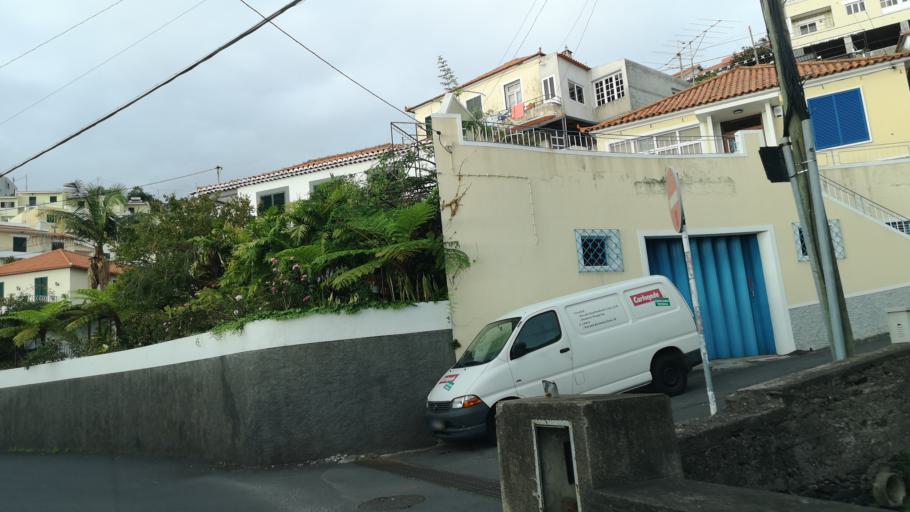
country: PT
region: Madeira
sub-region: Funchal
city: Nossa Senhora do Monte
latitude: 32.6581
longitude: -16.8948
